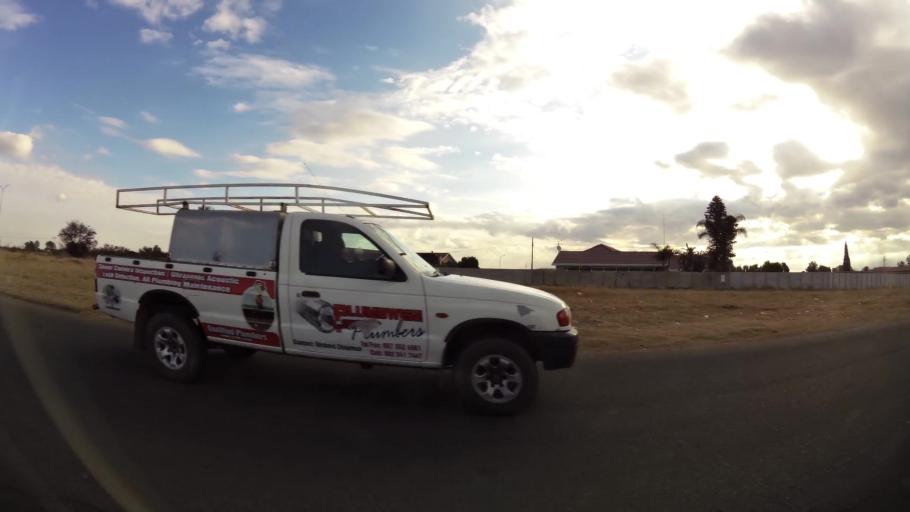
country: ZA
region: Orange Free State
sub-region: Lejweleputswa District Municipality
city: Welkom
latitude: -28.0026
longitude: 26.7358
